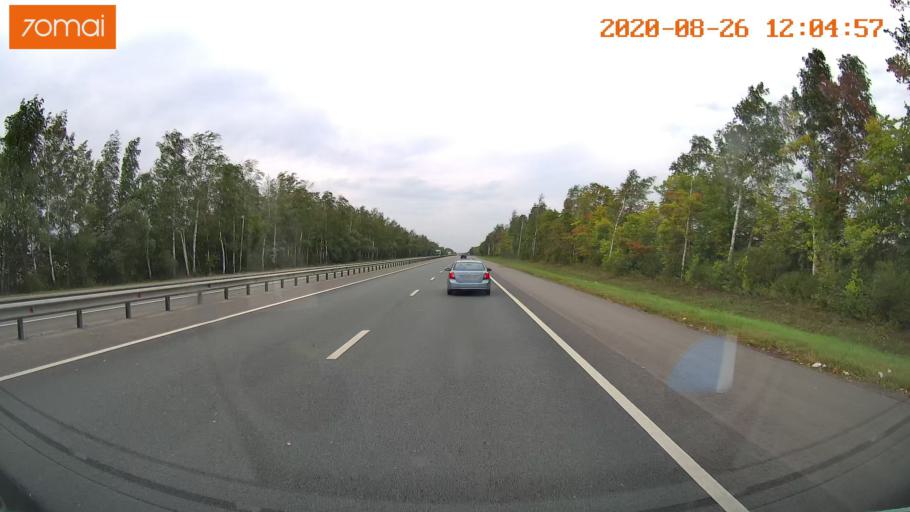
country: RU
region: Rjazan
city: Kiritsy
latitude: 54.3159
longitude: 40.1776
